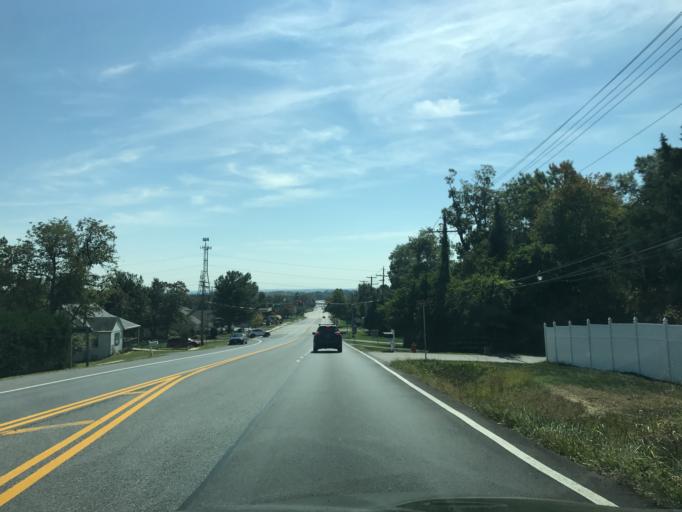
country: US
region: Maryland
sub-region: Howard County
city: Columbia
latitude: 39.2174
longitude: -76.8064
